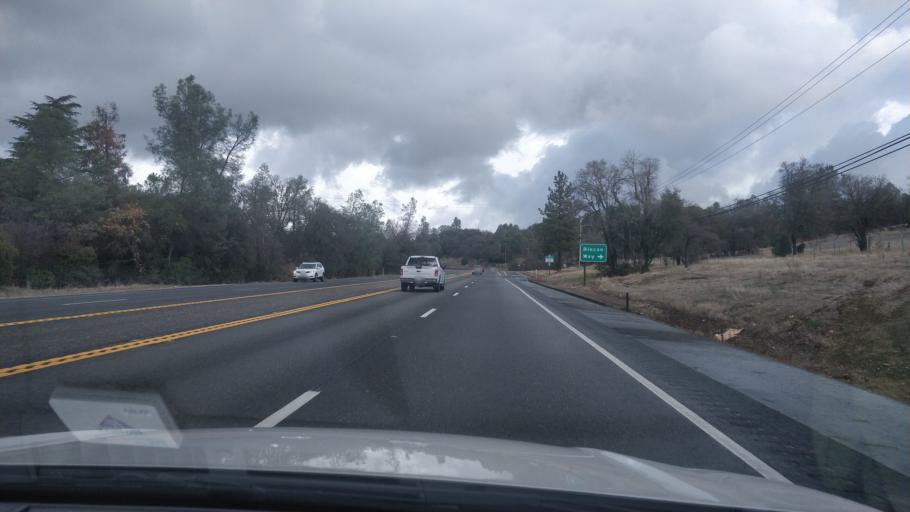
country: US
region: California
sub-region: Nevada County
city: Lake of the Pines
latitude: 39.0158
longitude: -121.1020
